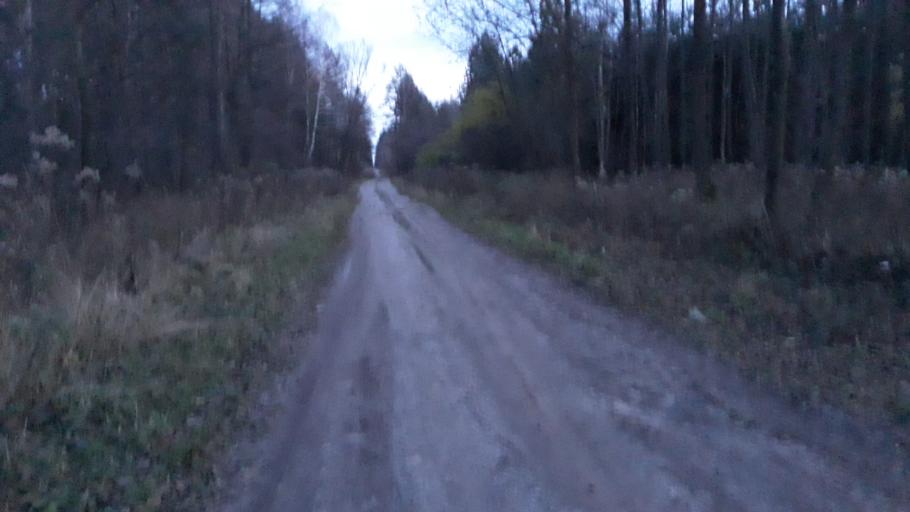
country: PL
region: Lublin Voivodeship
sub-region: Powiat janowski
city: Dzwola
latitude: 50.6585
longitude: 22.4946
